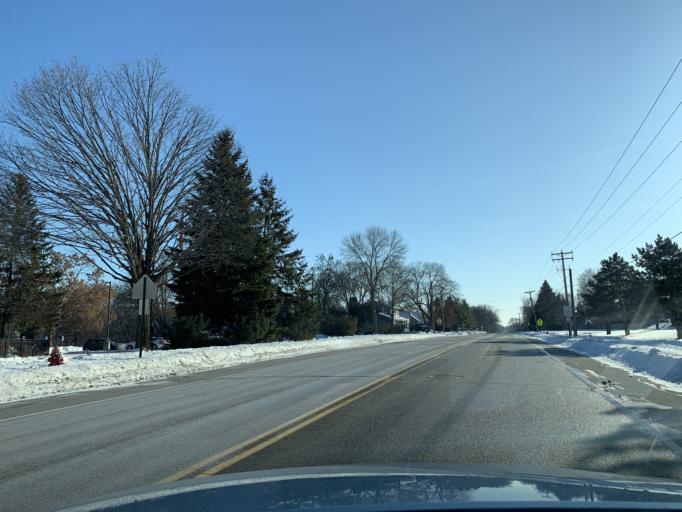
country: US
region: Minnesota
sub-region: Scott County
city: Savage
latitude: 44.8323
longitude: -93.3584
